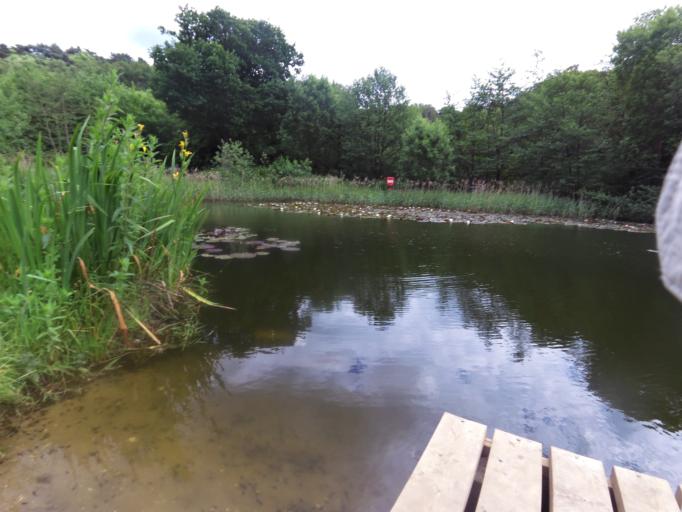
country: GB
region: England
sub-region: Norfolk
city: Sheringham
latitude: 52.9318
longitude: 1.1395
